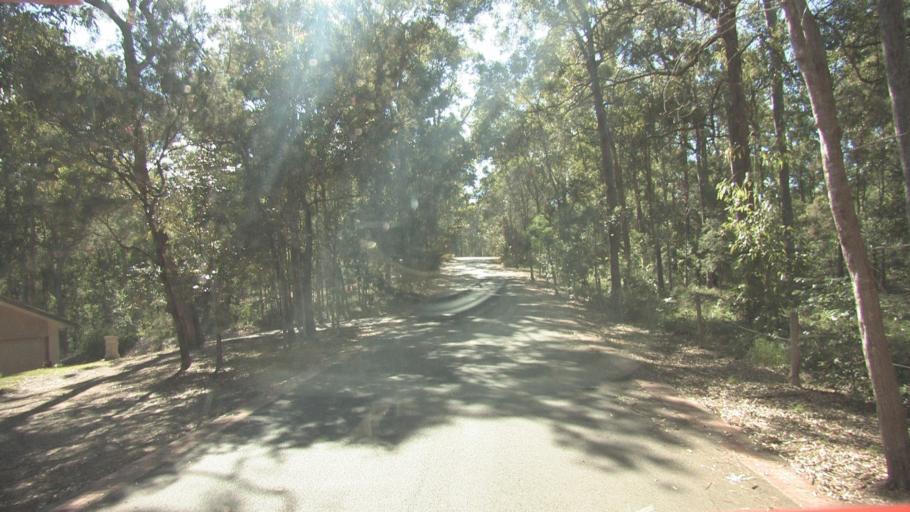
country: AU
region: Queensland
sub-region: Logan
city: Slacks Creek
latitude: -27.6363
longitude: 153.1833
